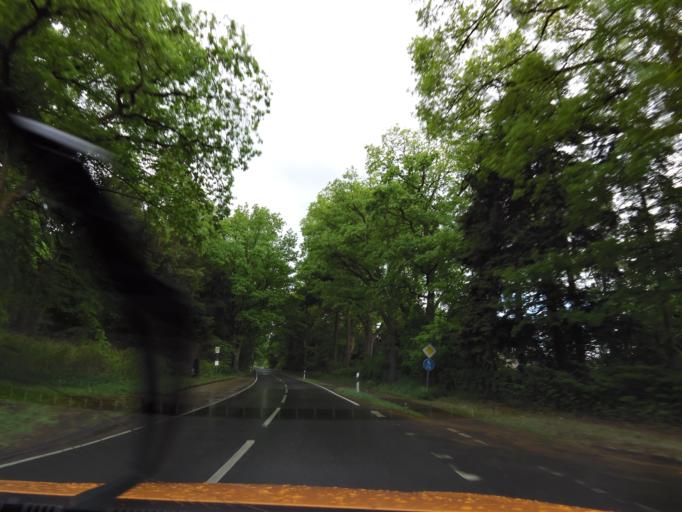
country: DE
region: Lower Saxony
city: Hude
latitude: 53.1222
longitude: 8.4301
